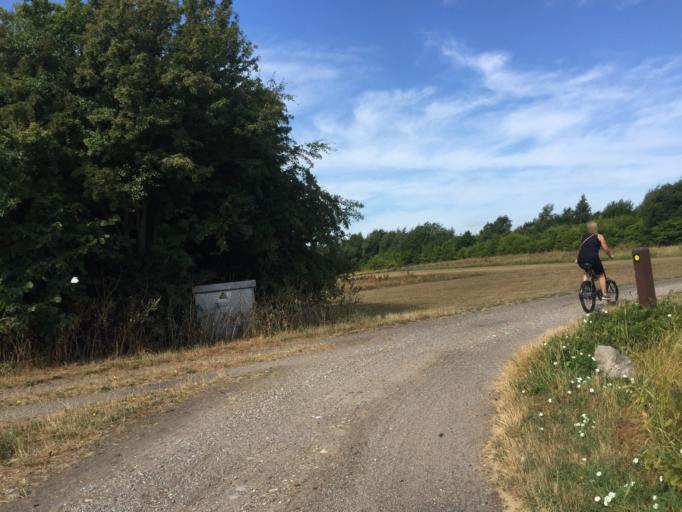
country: DK
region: Central Jutland
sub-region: Samso Kommune
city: Tranebjerg
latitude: 55.9569
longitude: 10.4120
